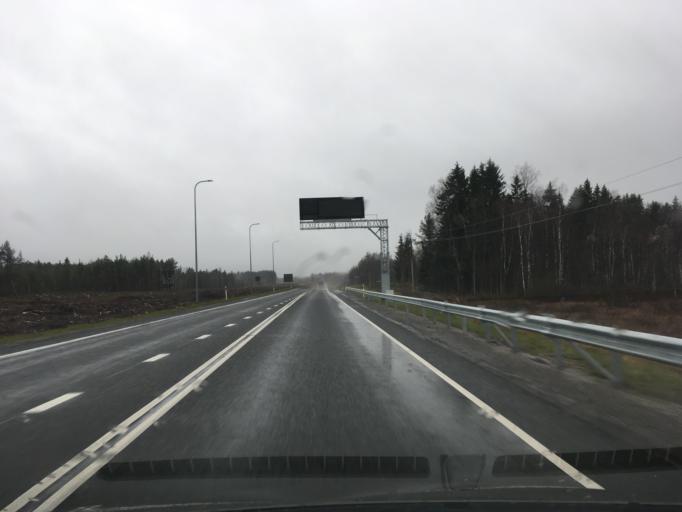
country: EE
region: Harju
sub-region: Nissi vald
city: Turba
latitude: 58.9918
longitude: 24.0584
